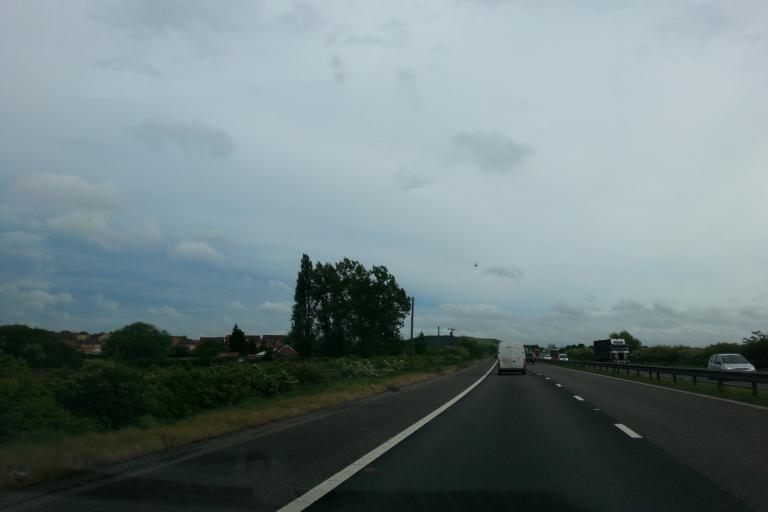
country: GB
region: England
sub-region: Doncaster
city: Tickhill
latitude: 53.4212
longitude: -1.0902
